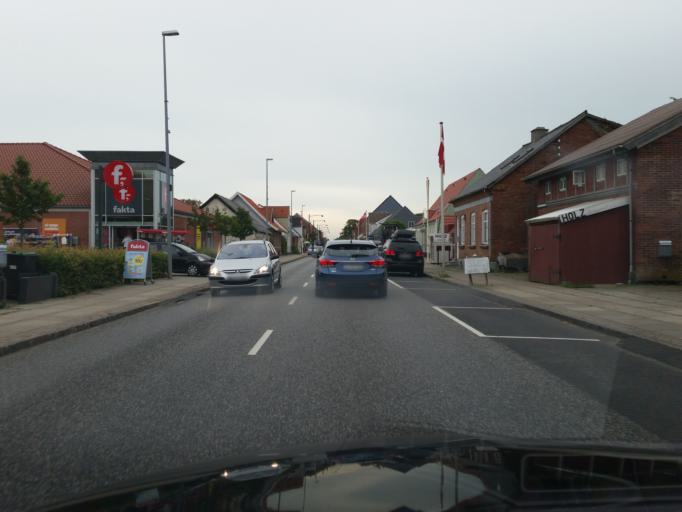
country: DK
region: South Denmark
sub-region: Varde Kommune
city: Oksbol
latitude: 55.7800
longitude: 8.2854
